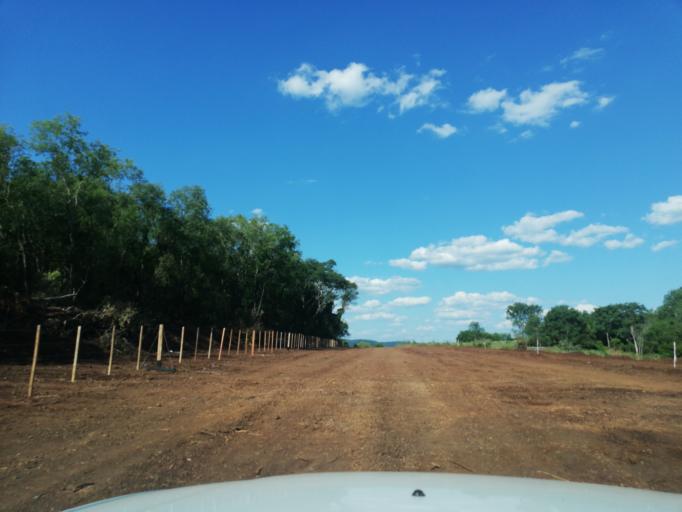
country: AR
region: Misiones
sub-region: Departamento de Candelaria
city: Candelaria
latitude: -27.5561
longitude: -55.7047
